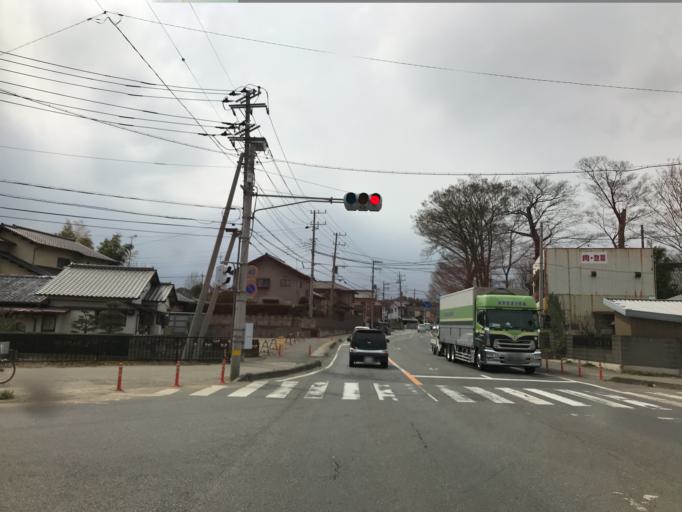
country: JP
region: Ibaraki
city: Moriya
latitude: 35.9812
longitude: 140.0535
